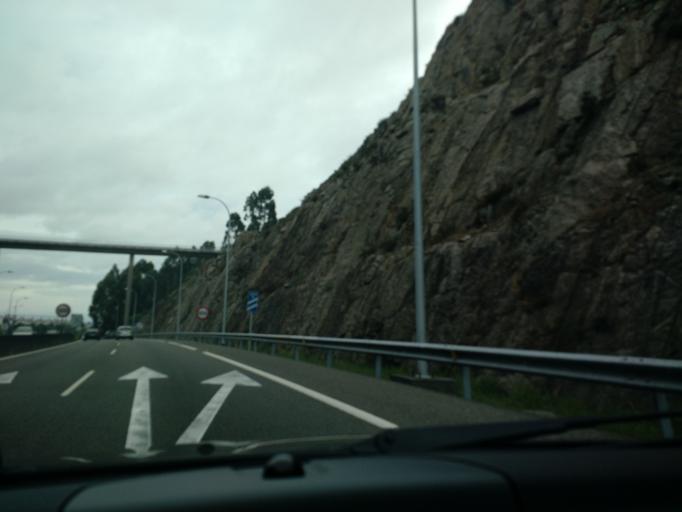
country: ES
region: Galicia
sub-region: Provincia da Coruna
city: Culleredo
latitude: 43.3237
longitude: -8.3929
